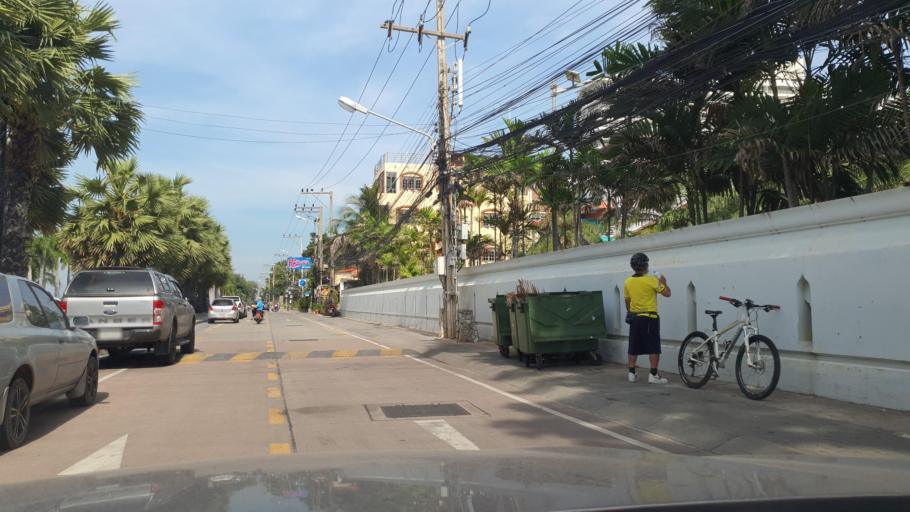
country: TH
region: Chon Buri
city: Phatthaya
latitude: 12.8991
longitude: 100.8665
